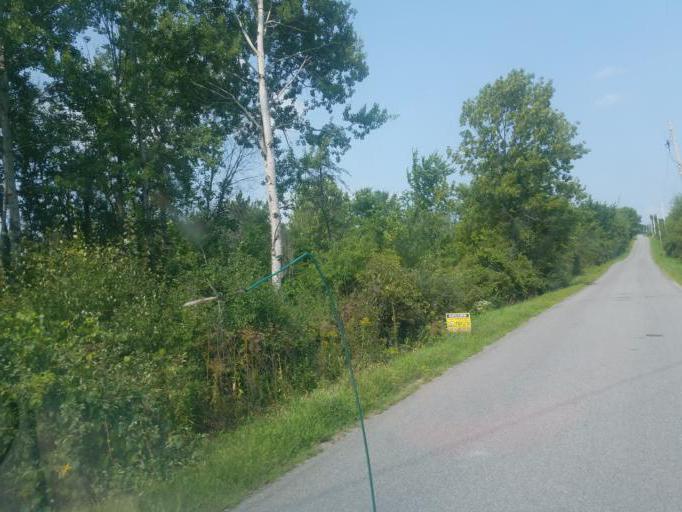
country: US
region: New York
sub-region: Montgomery County
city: Wellsville
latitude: 42.8609
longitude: -74.3314
